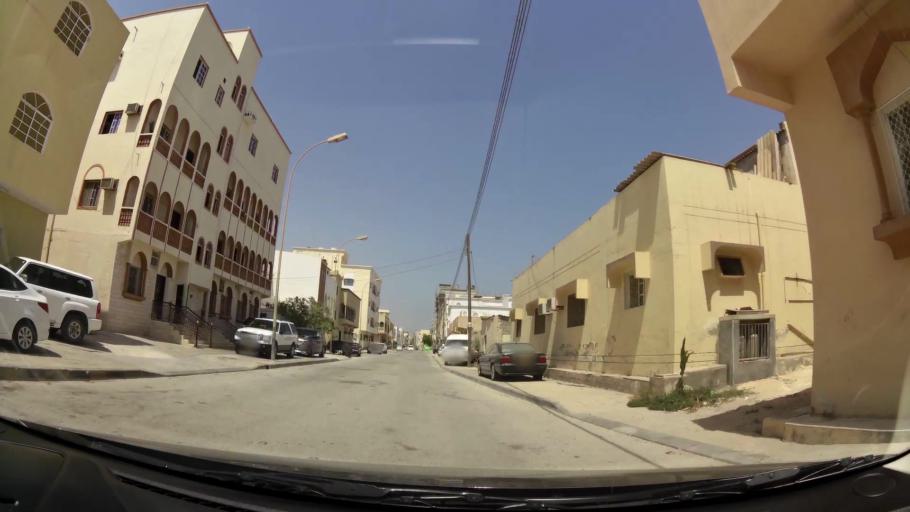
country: OM
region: Zufar
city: Salalah
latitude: 17.0164
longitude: 54.0869
